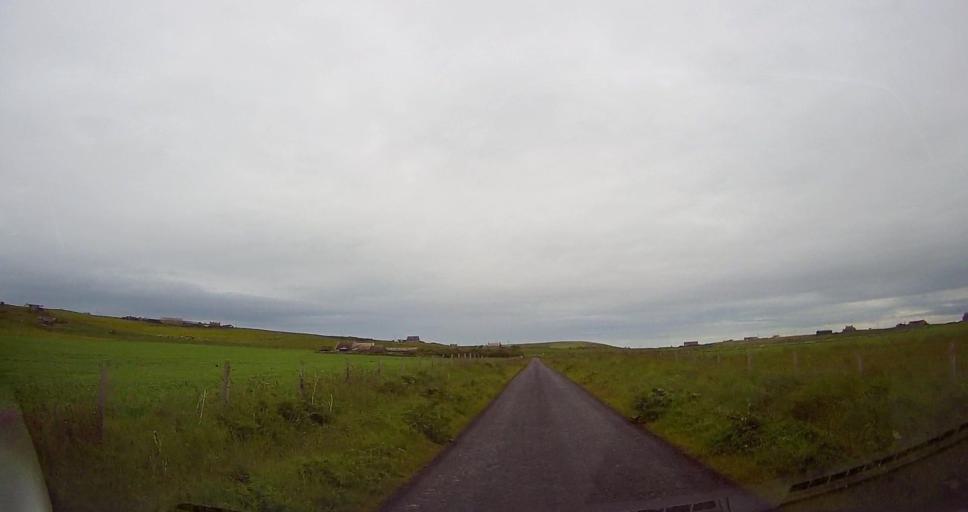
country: GB
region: Scotland
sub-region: Orkney Islands
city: Stromness
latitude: 59.1267
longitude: -3.2917
